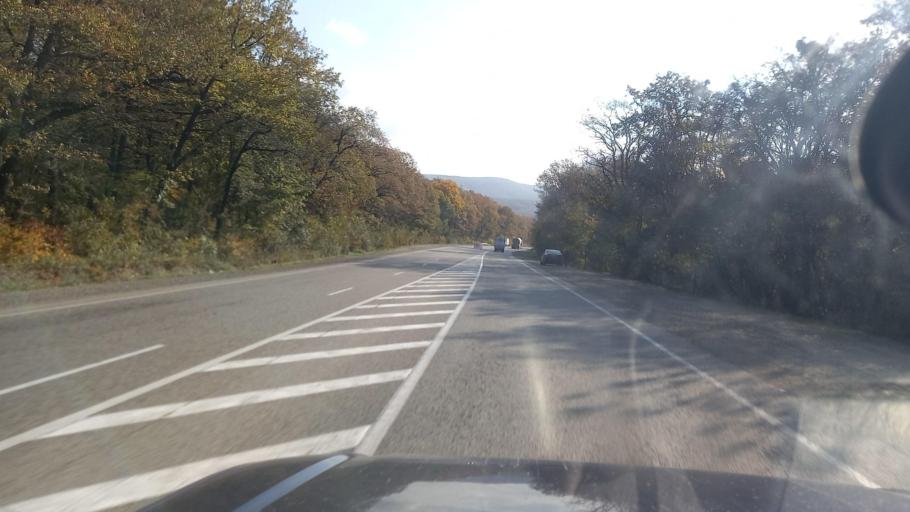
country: RU
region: Krasnodarskiy
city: Verkhnebakanskiy
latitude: 44.8429
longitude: 37.6994
